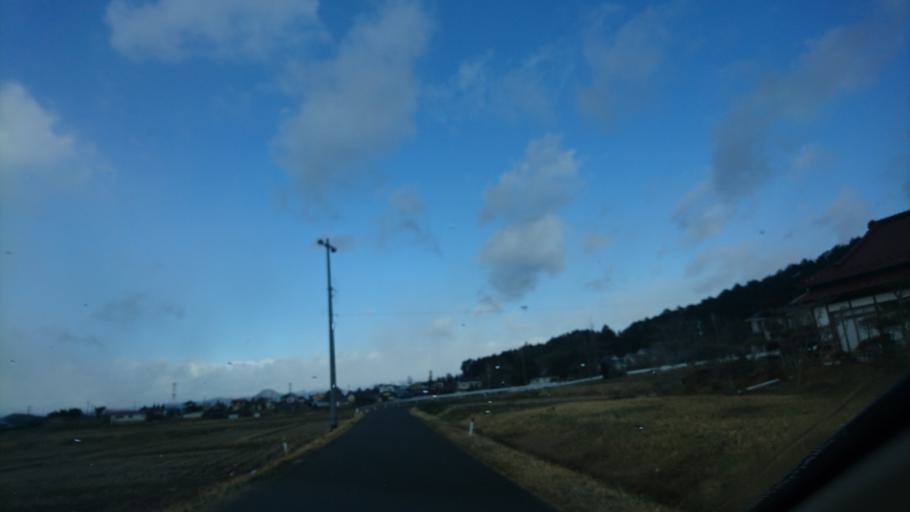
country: JP
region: Iwate
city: Ichinoseki
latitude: 38.7944
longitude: 141.0272
